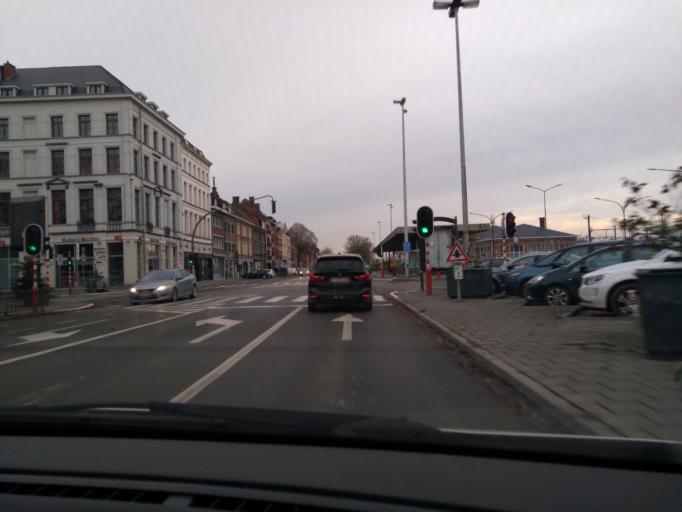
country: BE
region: Wallonia
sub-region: Province du Hainaut
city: Tournai
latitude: 50.6125
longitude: 3.3964
